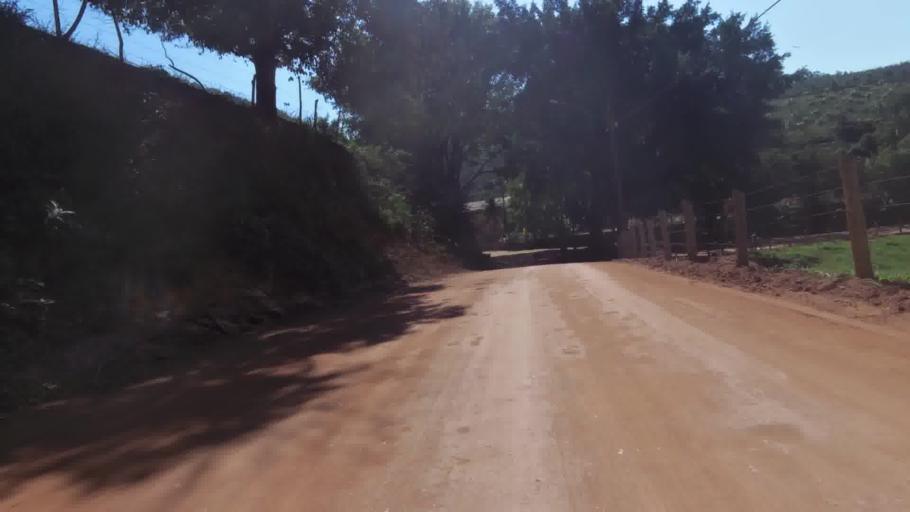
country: BR
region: Espirito Santo
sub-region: Alfredo Chaves
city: Alfredo Chaves
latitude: -20.6316
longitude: -40.7645
